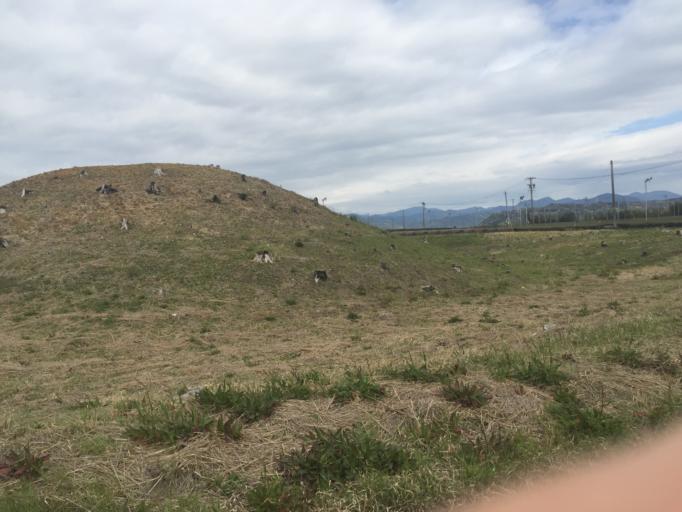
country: JP
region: Shizuoka
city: Mori
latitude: 34.7973
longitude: 137.9470
